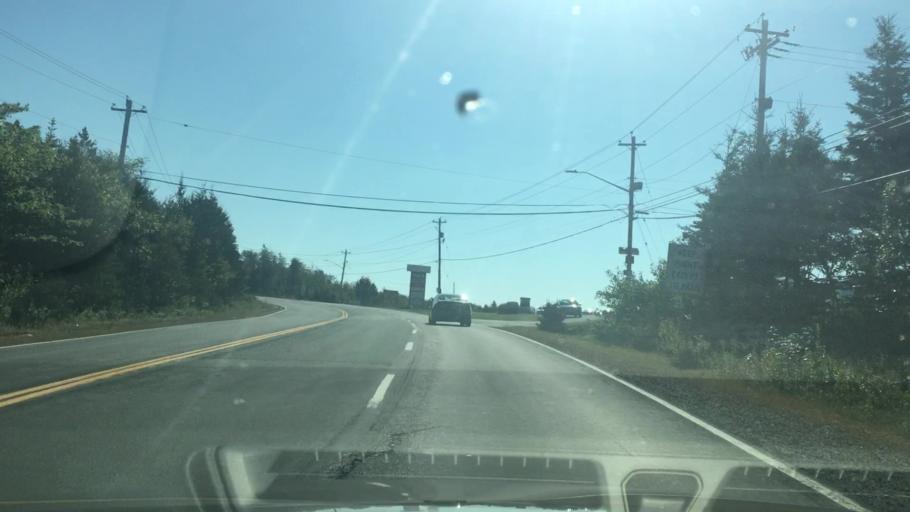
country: CA
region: Nova Scotia
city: Cole Harbour
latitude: 44.7787
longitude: -63.0925
